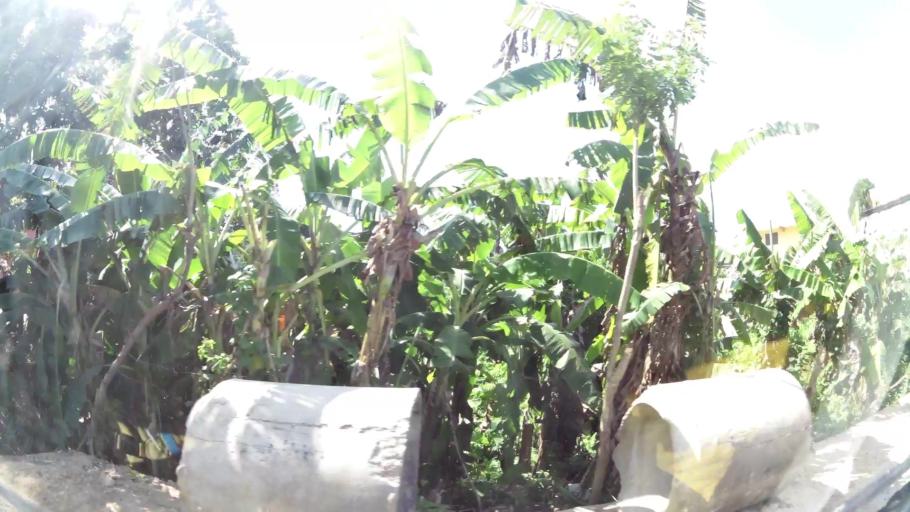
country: DO
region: San Cristobal
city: San Cristobal
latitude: 18.4273
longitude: -70.0818
